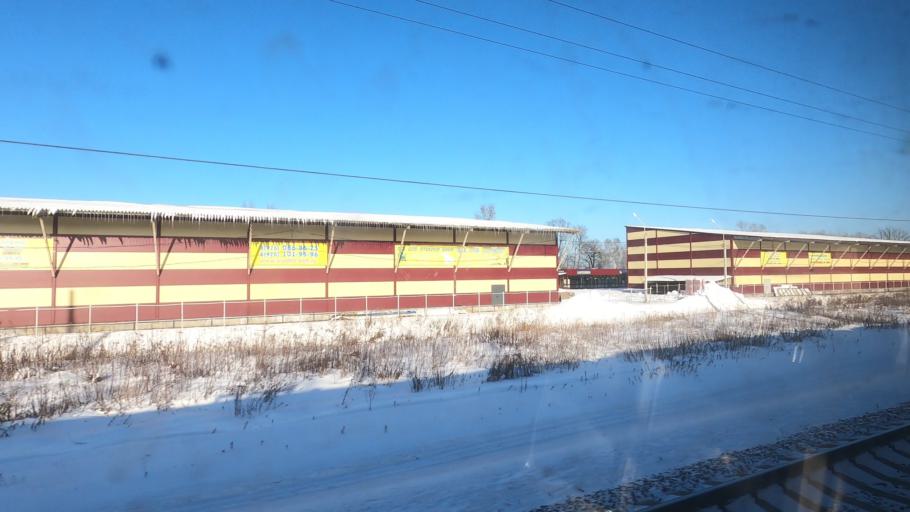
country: RU
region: Moskovskaya
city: Imeni Vorovskogo
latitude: 55.7216
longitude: 38.3200
